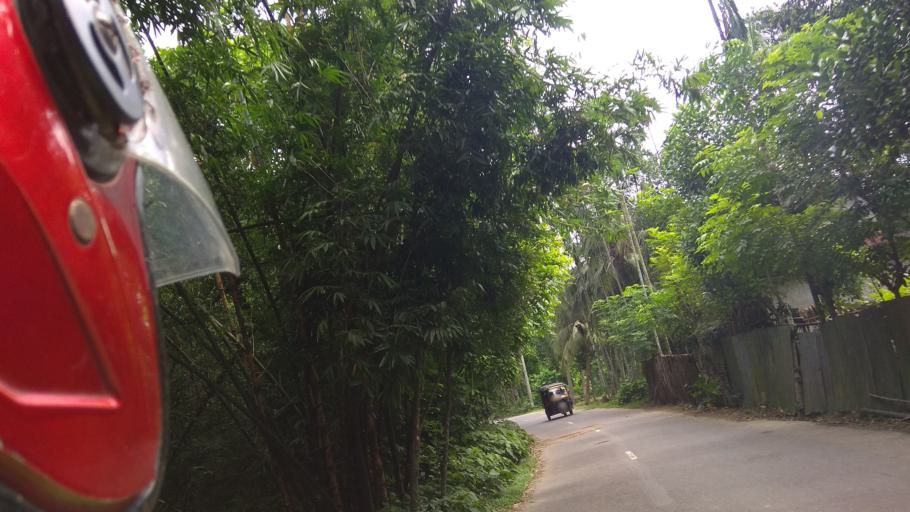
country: BD
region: Khulna
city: Kalia
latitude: 23.1363
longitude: 89.6443
